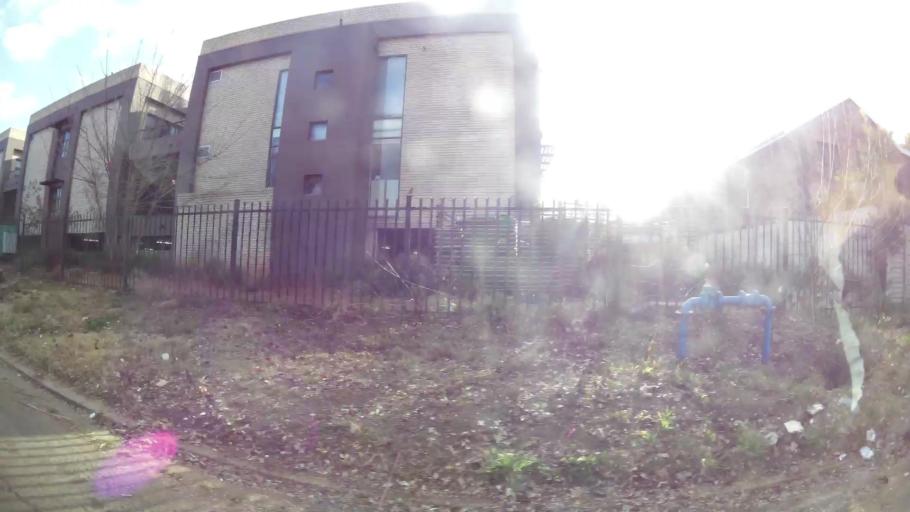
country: ZA
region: Orange Free State
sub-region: Mangaung Metropolitan Municipality
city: Bloemfontein
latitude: -29.1054
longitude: 26.1949
